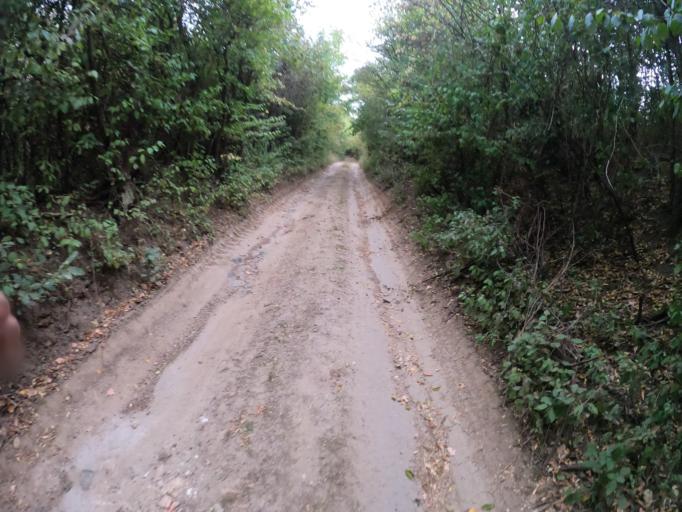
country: HU
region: Veszprem
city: Revfueloep
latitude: 46.8940
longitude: 17.5588
